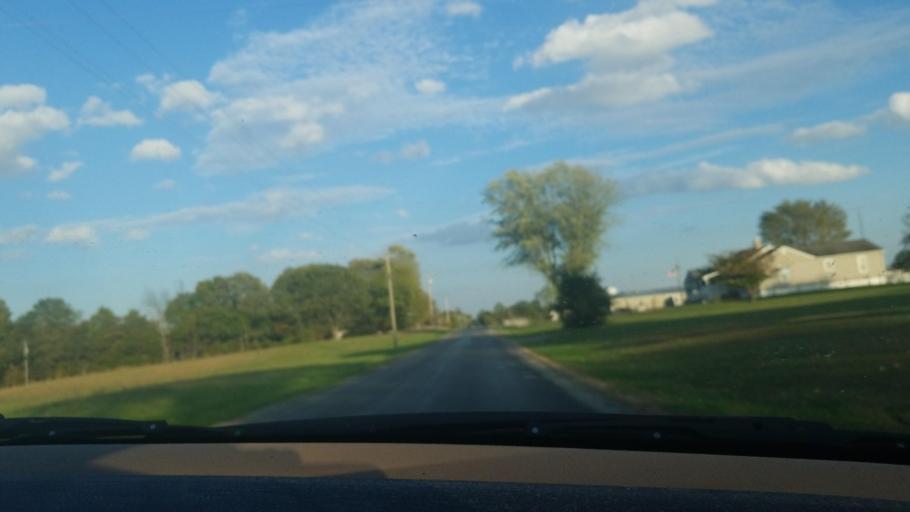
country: US
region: Illinois
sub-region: Saline County
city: Carrier Mills
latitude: 37.7719
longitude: -88.7409
